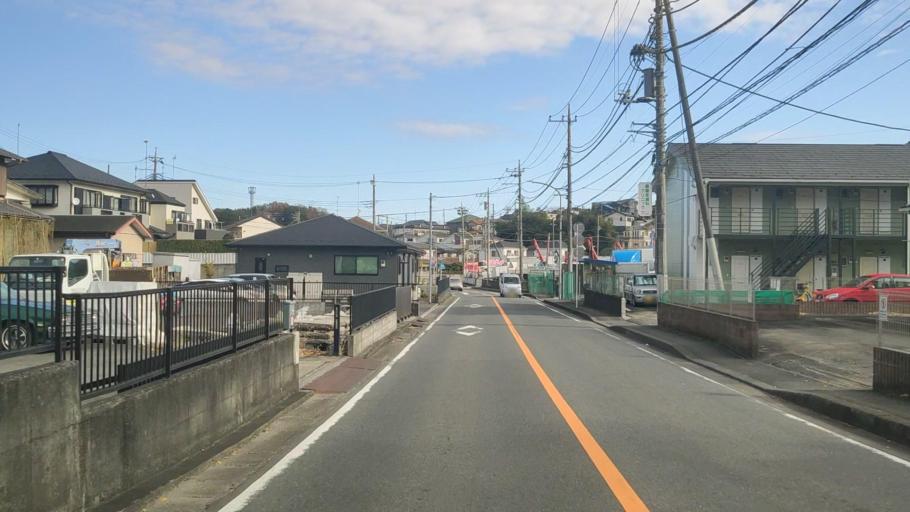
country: JP
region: Kanagawa
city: Minami-rinkan
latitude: 35.4544
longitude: 139.5373
